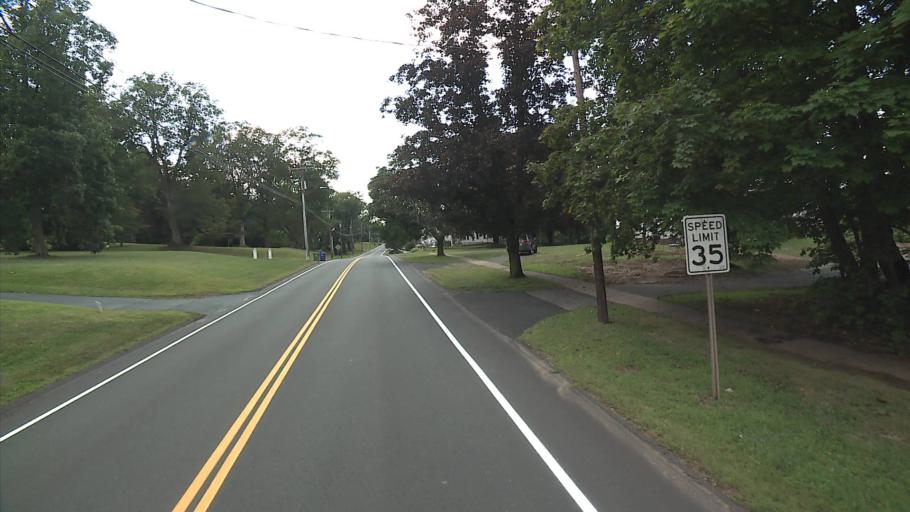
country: US
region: Connecticut
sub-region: Middlesex County
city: Cromwell
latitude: 41.5904
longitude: -72.6250
